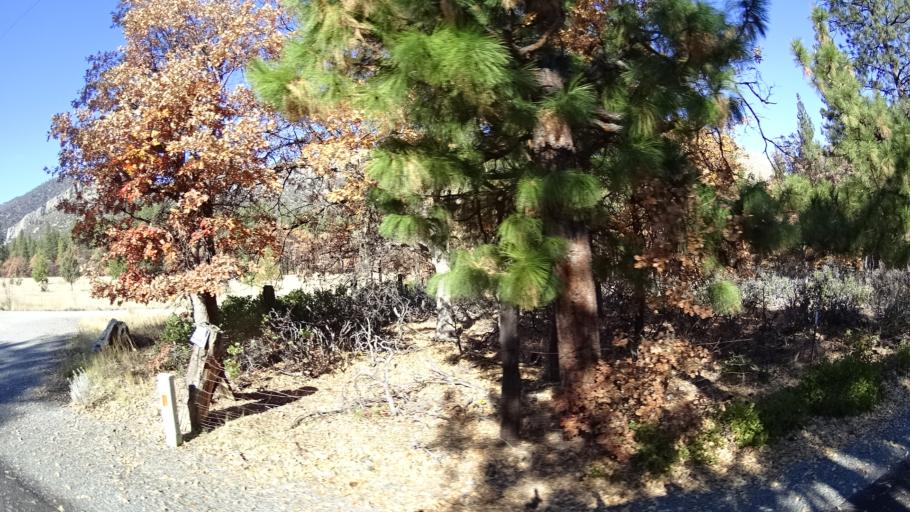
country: US
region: California
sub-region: Siskiyou County
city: Weed
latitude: 41.5035
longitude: -122.5829
